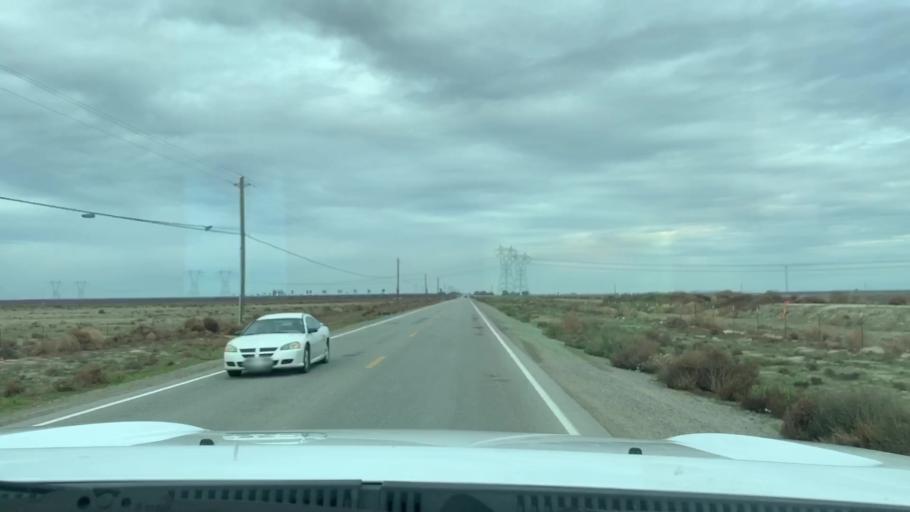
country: US
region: California
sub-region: Kern County
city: Rosedale
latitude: 35.2746
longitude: -119.2526
